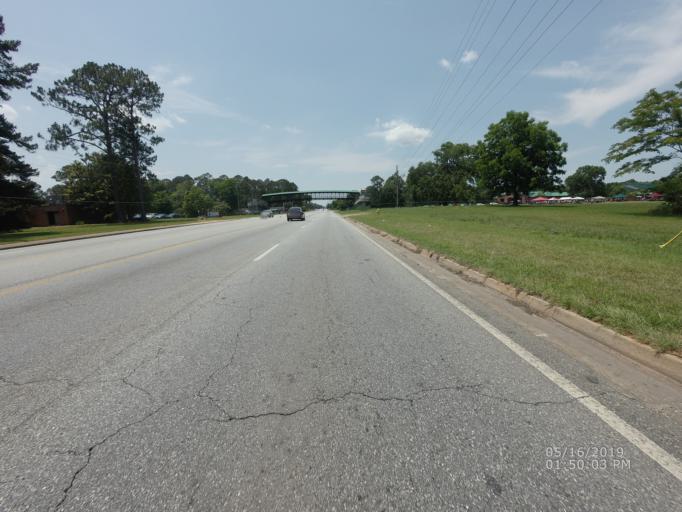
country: US
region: Georgia
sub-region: Dougherty County
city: Albany
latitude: 31.5492
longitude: -84.1894
